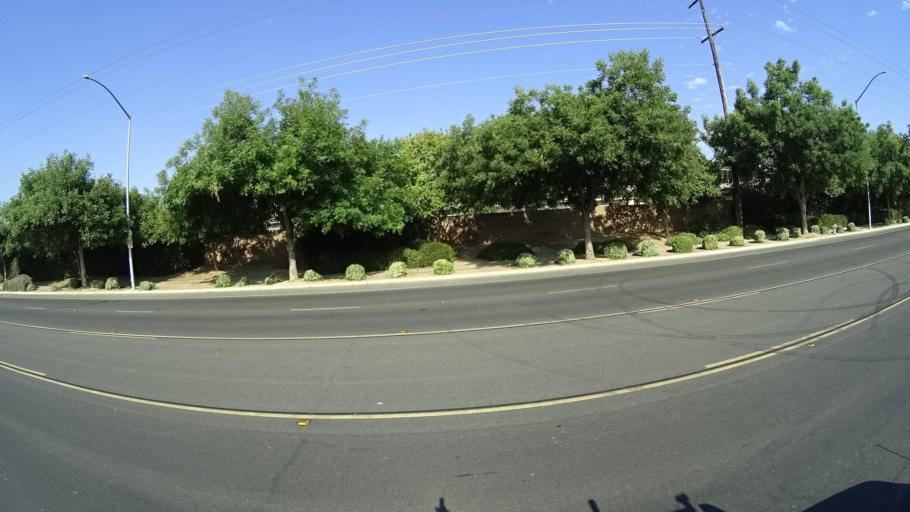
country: US
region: California
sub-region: Fresno County
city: Sunnyside
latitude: 36.7132
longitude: -119.6909
